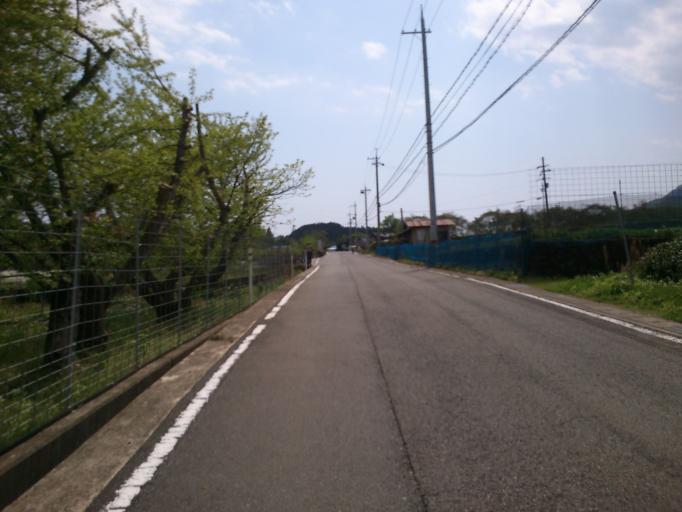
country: JP
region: Kyoto
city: Fukuchiyama
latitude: 35.3400
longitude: 134.9228
